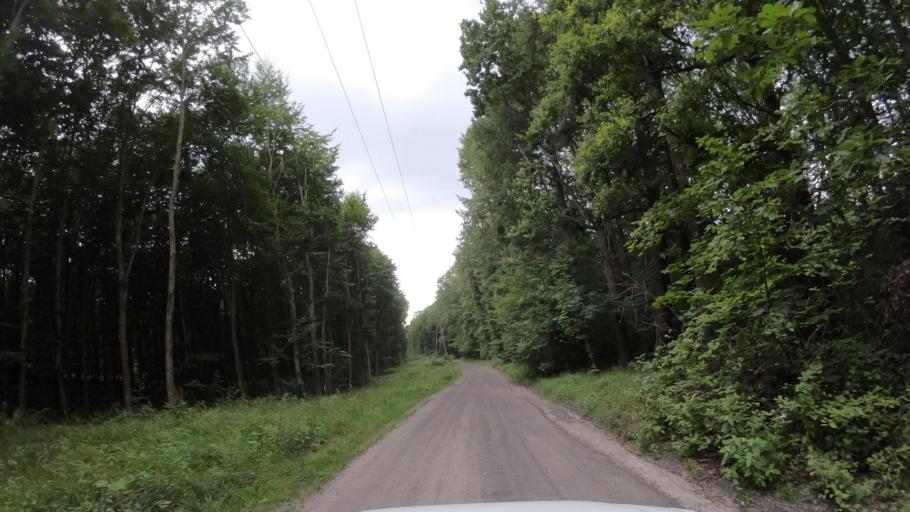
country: PL
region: West Pomeranian Voivodeship
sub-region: Powiat stargardzki
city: Dolice
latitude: 53.1973
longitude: 15.2753
